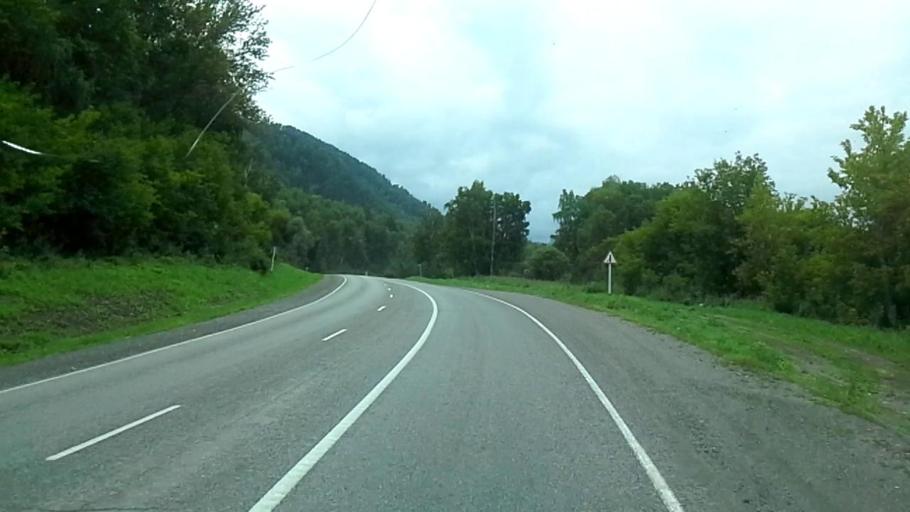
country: RU
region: Altay
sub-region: Mayminskiy Rayon
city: Manzherok
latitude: 51.8624
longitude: 85.7610
